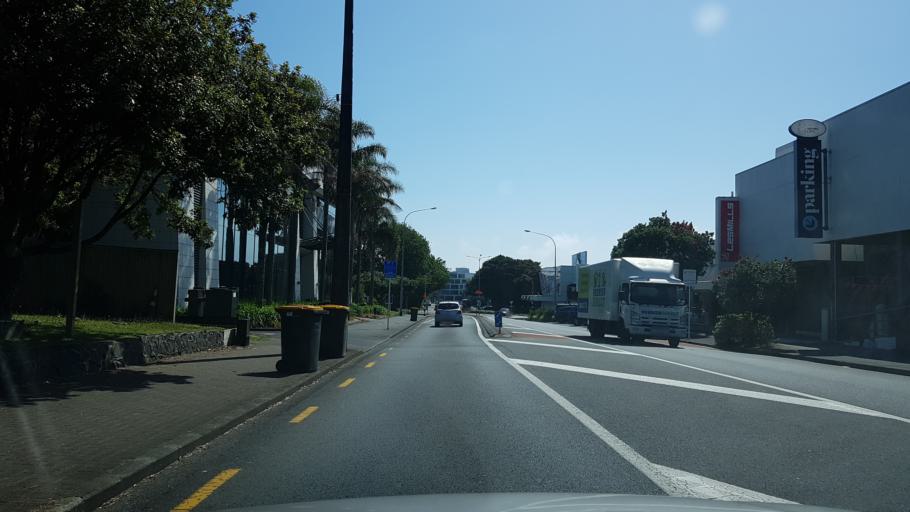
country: NZ
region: Auckland
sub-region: Auckland
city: North Shore
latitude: -36.7877
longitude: 174.7692
